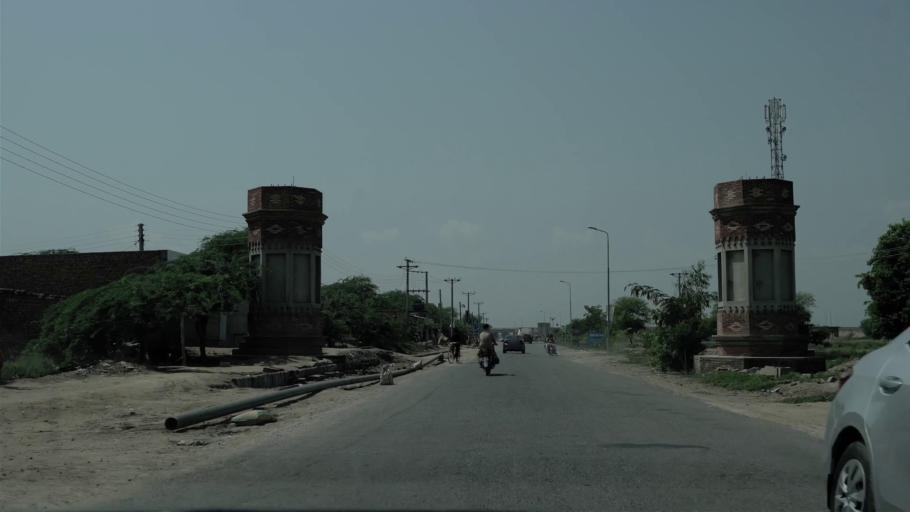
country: PK
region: Punjab
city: Gojra
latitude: 31.1770
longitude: 72.6312
